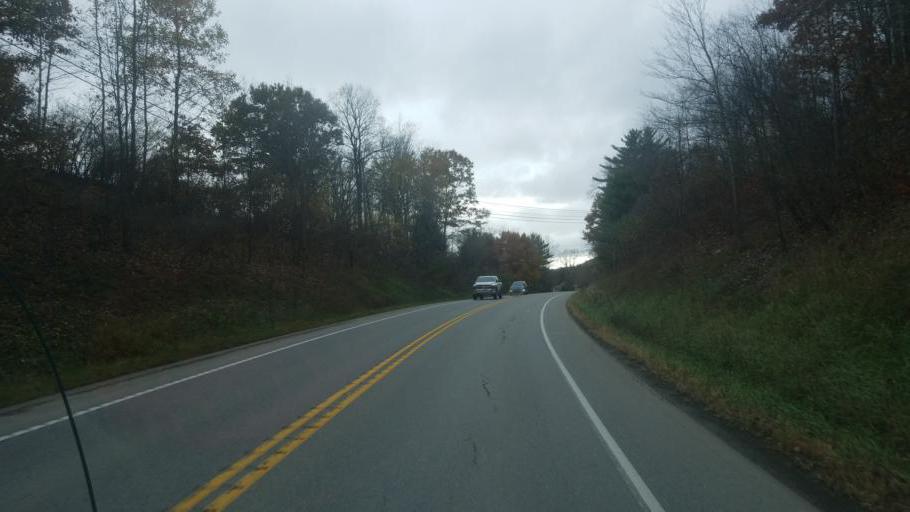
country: US
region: Pennsylvania
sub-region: Jefferson County
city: Brockway
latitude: 41.2738
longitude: -78.7079
